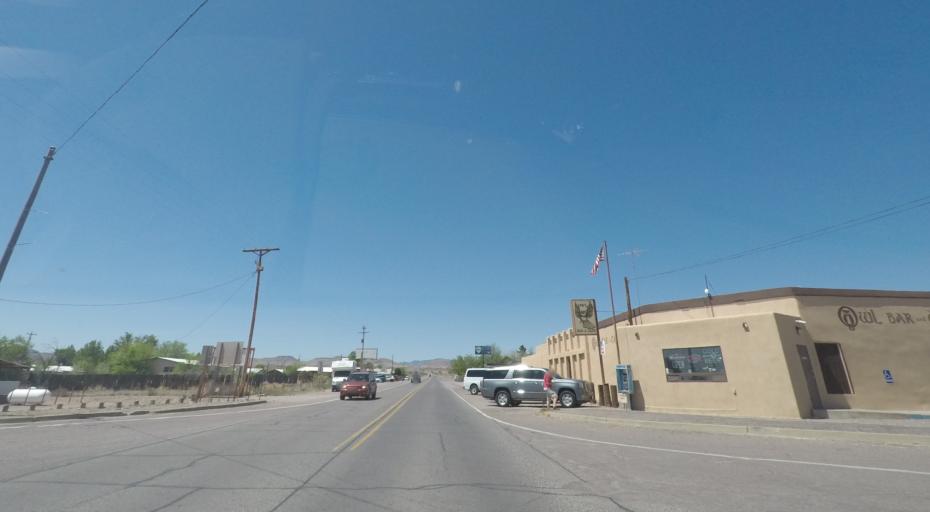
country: US
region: New Mexico
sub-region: Socorro County
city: Socorro
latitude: 33.9178
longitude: -106.8674
